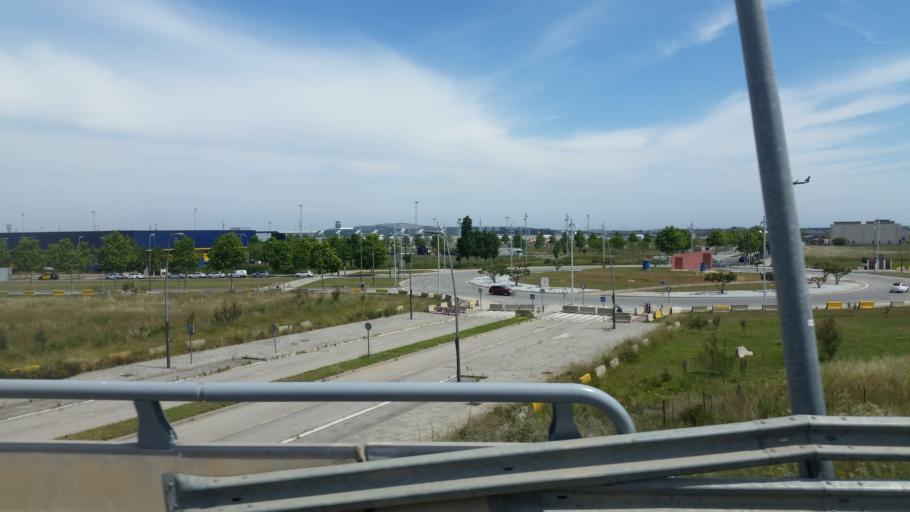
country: ES
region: Catalonia
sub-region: Provincia de Barcelona
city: Viladecans
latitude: 41.3002
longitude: 2.0530
